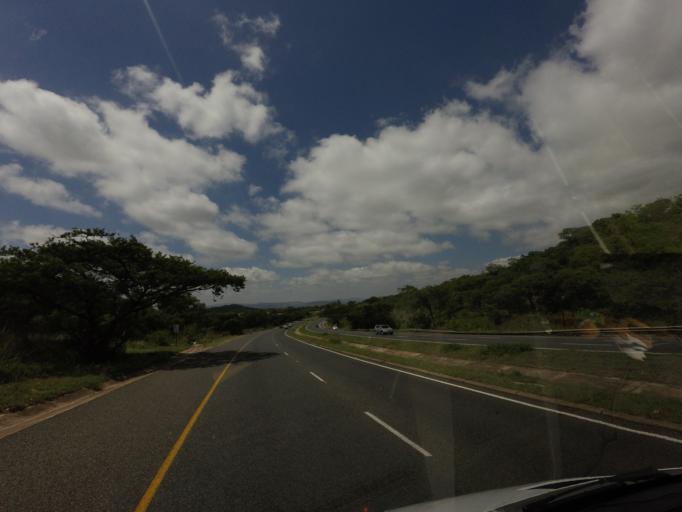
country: ZA
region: Mpumalanga
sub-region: Ehlanzeni District
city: White River
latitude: -25.3997
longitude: 30.9830
